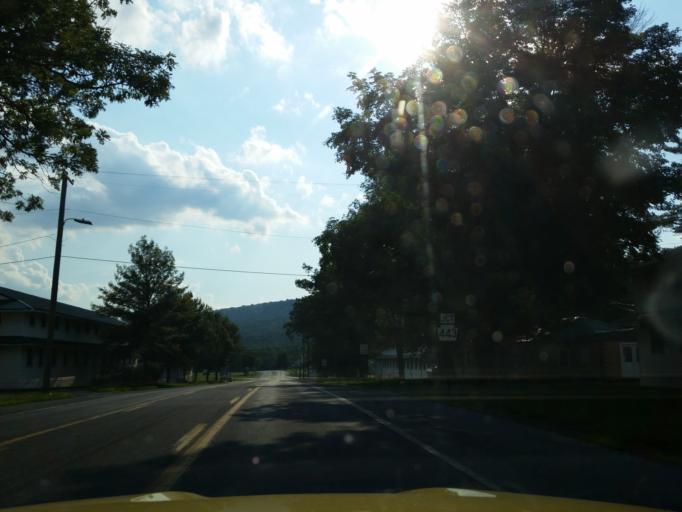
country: US
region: Pennsylvania
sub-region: Lebanon County
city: Jonestown
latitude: 40.4318
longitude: -76.5884
